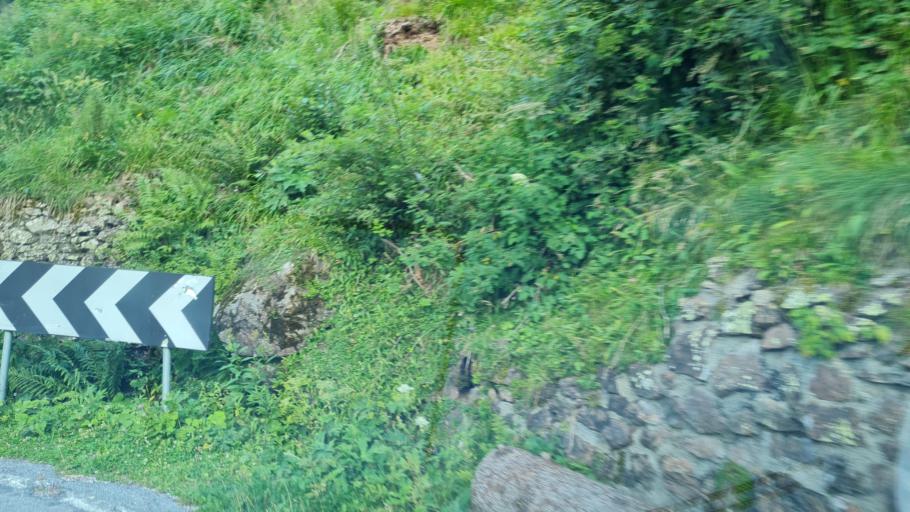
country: IT
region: Trentino-Alto Adige
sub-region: Provincia di Trento
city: Palu del Fersina
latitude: 46.1693
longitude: 11.4351
